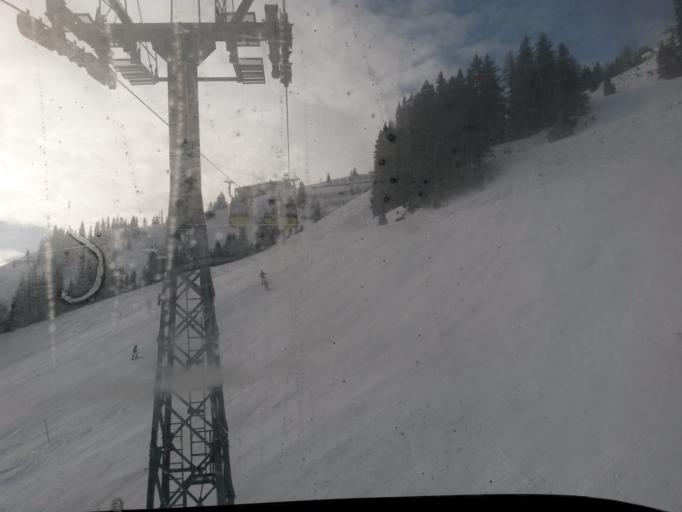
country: AT
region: Salzburg
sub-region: Politischer Bezirk Sankt Johann im Pongau
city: Dorfgastein
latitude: 47.2330
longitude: 13.1741
